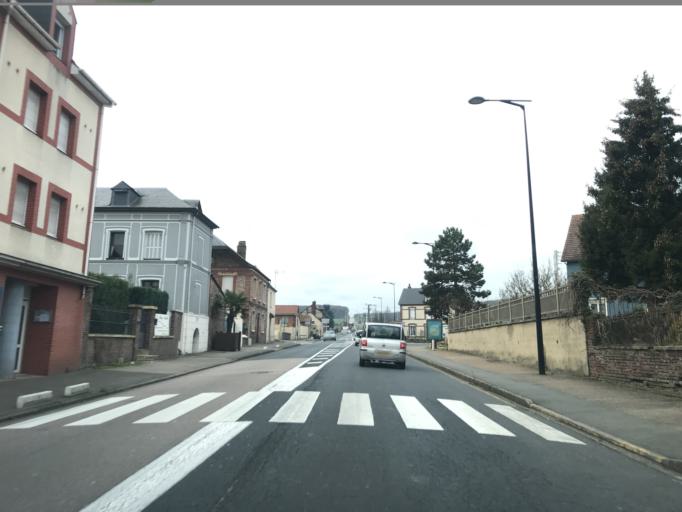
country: FR
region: Haute-Normandie
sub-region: Departement de l'Eure
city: Fleury-sur-Andelle
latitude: 49.3633
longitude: 1.3538
